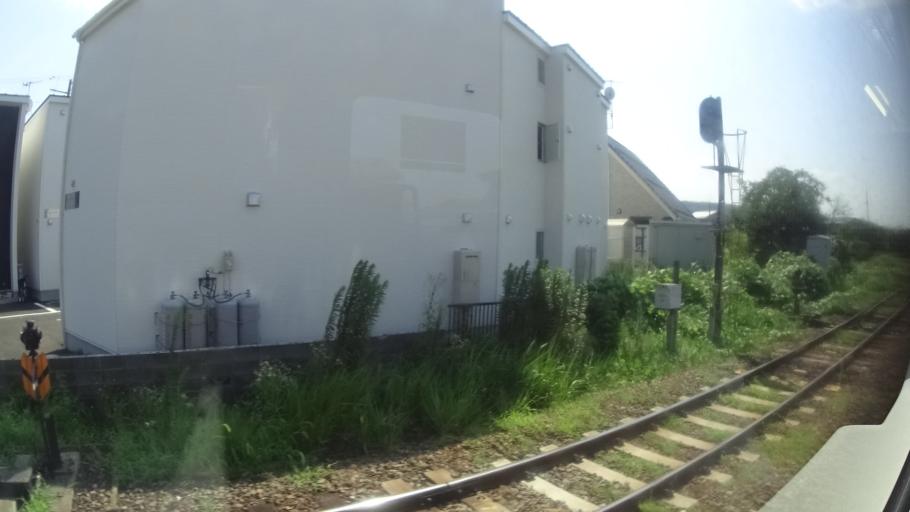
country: JP
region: Miyagi
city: Wakuya
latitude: 38.5128
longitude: 141.1923
